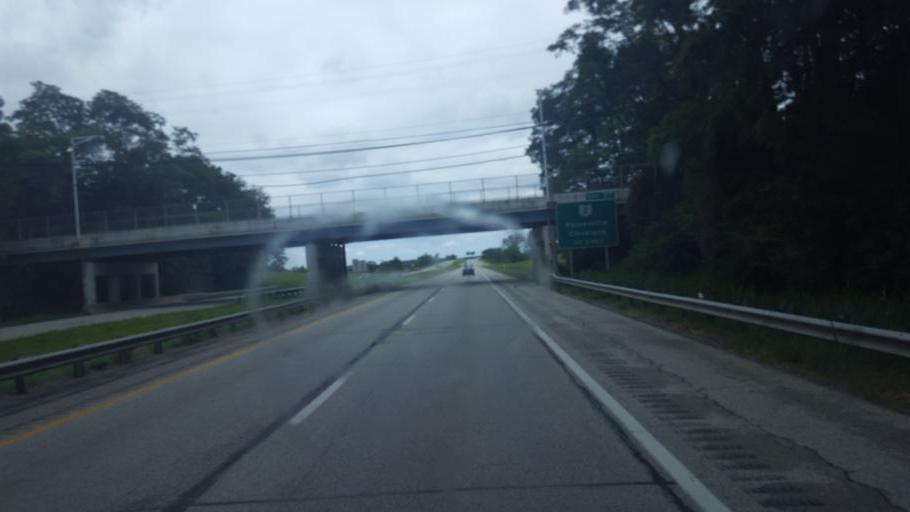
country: US
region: Ohio
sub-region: Lake County
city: Painesville
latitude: 41.7091
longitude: -81.2686
